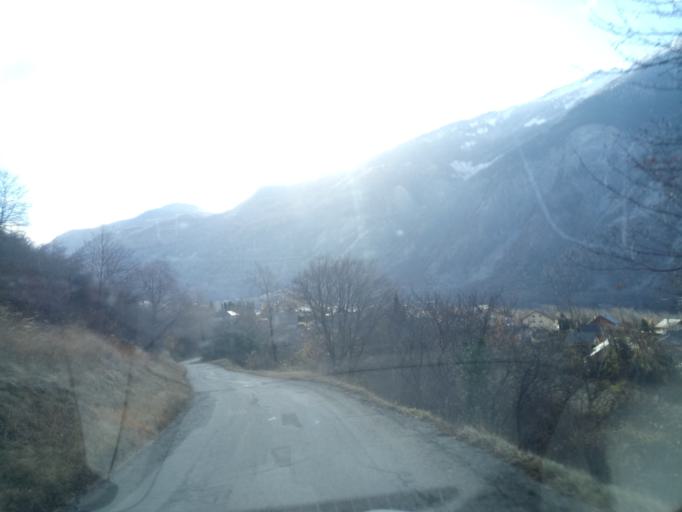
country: FR
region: Rhone-Alpes
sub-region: Departement de la Savoie
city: Villargondran
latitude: 45.2614
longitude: 6.3940
